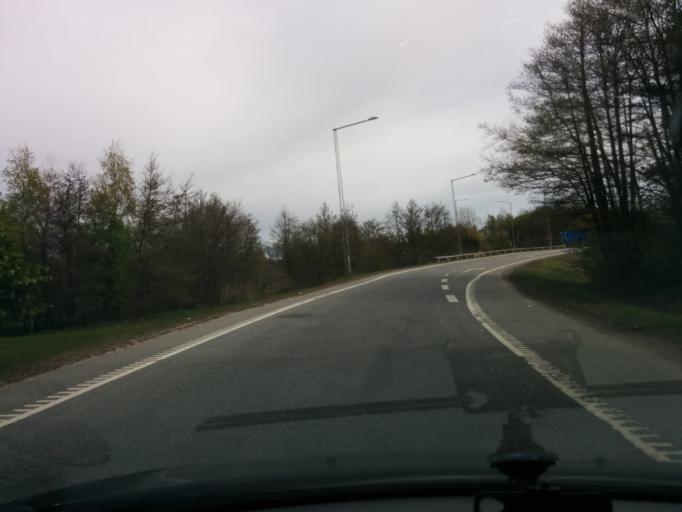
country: SE
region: Stockholm
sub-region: Botkyrka Kommun
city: Alby
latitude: 59.2449
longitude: 17.8402
